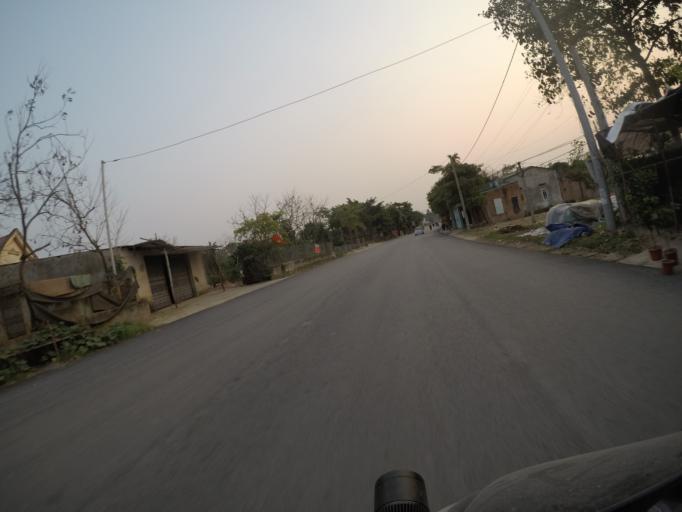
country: VN
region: Vinh Phuc
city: Trai Ngau
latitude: 21.4429
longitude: 105.5731
